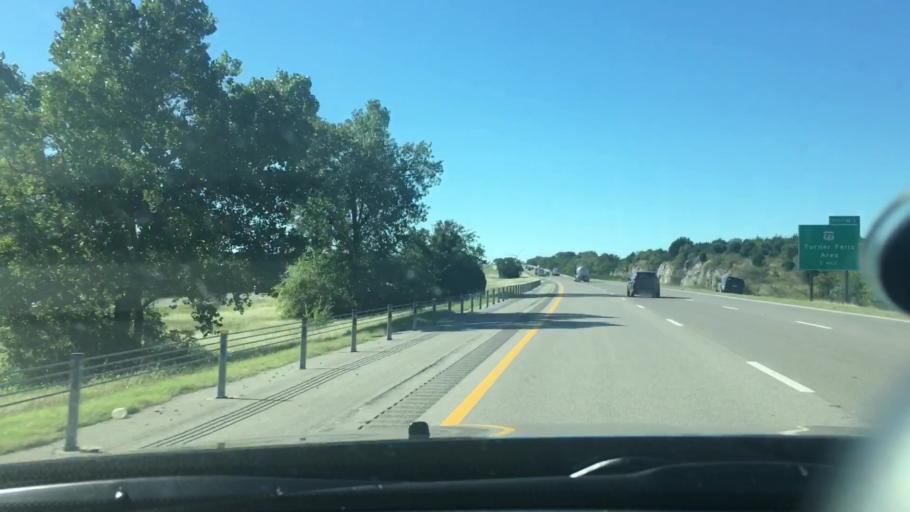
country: US
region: Oklahoma
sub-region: Murray County
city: Davis
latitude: 34.4176
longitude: -97.1373
